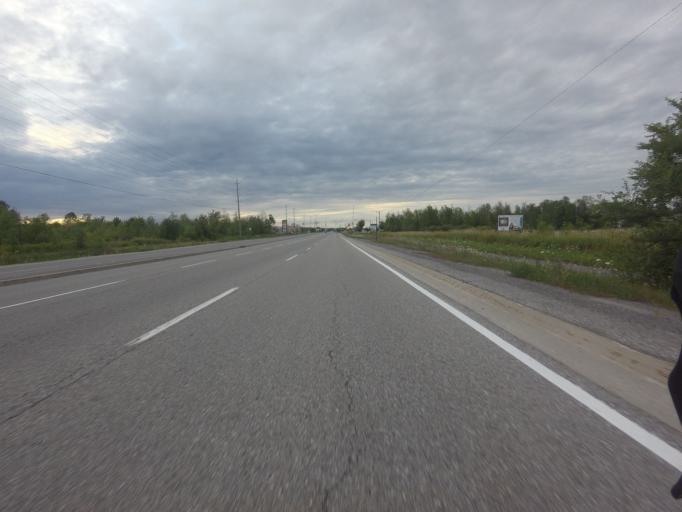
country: CA
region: Ontario
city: Carleton Place
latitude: 45.1385
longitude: -76.1253
